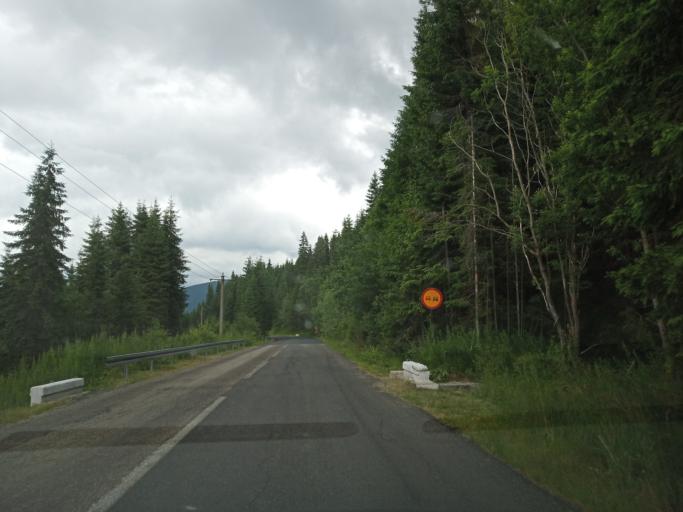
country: RO
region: Gorj
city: Novaci-Straini
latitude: 45.4248
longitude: 23.6897
